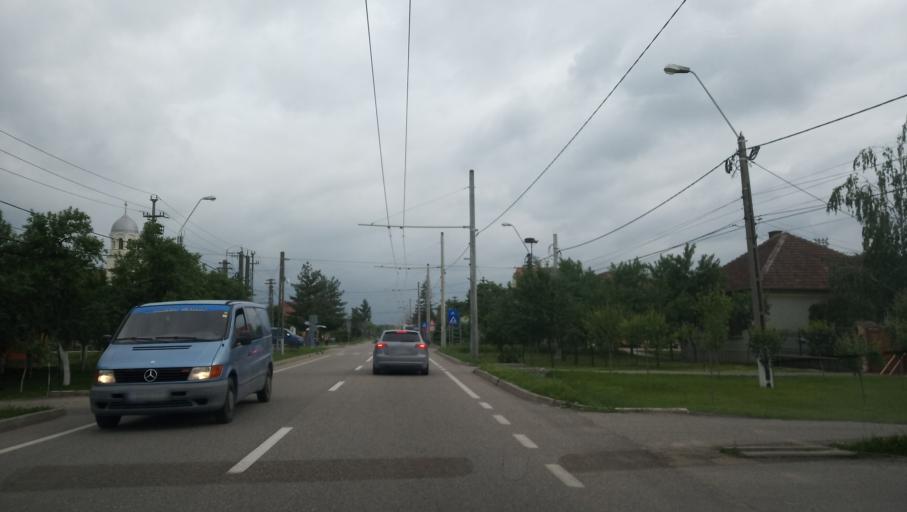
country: RO
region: Timis
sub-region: Comuna Ghiroda
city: Ghiroda
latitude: 45.7714
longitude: 21.3023
